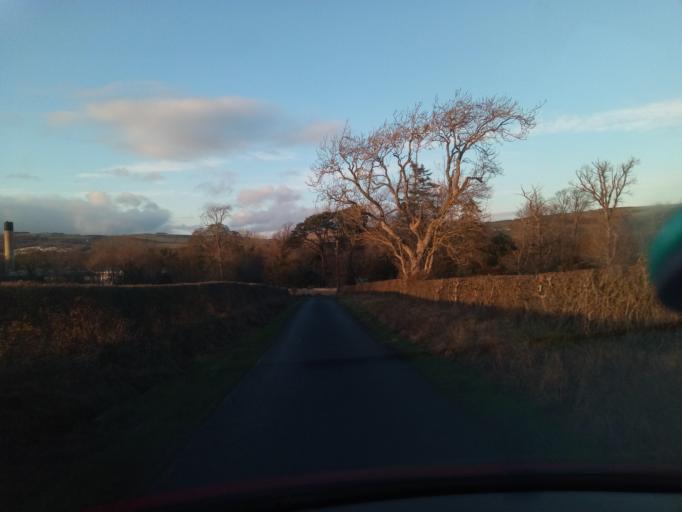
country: GB
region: Scotland
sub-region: The Scottish Borders
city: Melrose
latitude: 55.5941
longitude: -2.7374
